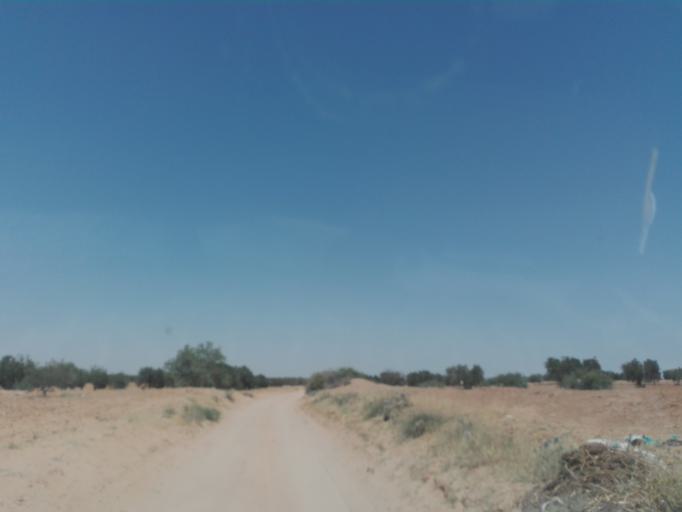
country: TN
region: Safaqis
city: Bi'r `Ali Bin Khalifah
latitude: 34.6726
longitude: 10.2301
